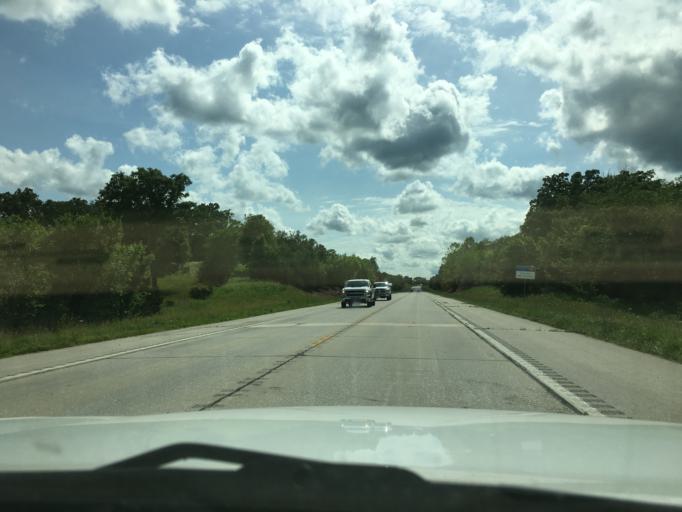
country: US
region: Missouri
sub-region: Franklin County
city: Gerald
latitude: 38.4157
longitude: -91.3001
